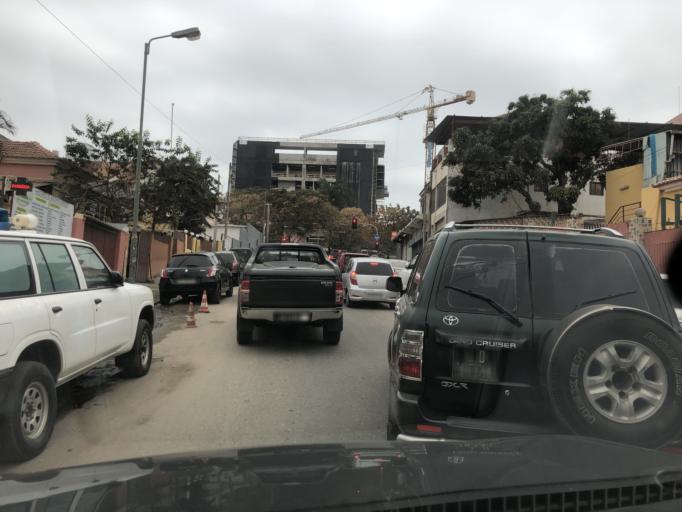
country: AO
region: Luanda
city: Luanda
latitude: -8.8259
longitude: 13.2284
